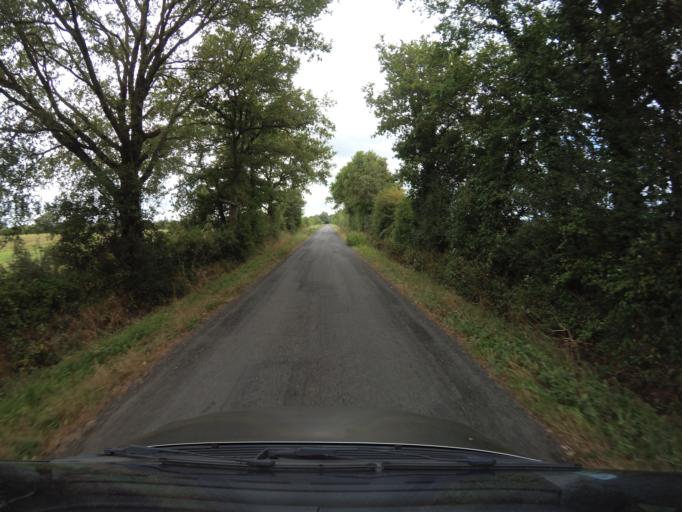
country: FR
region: Pays de la Loire
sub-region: Departement de la Vendee
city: Saint-Philbert-de-Bouaine
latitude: 46.9974
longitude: -1.5178
